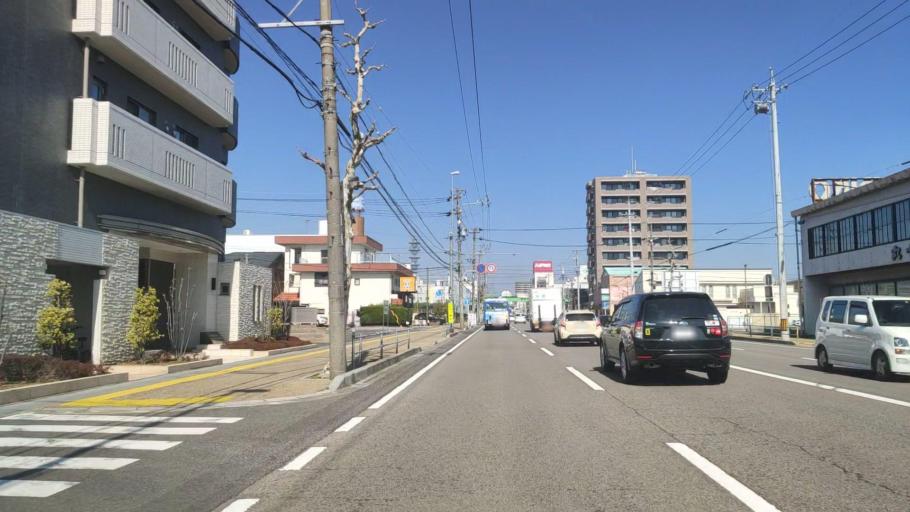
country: JP
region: Gifu
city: Gifu-shi
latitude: 35.4034
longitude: 136.7474
